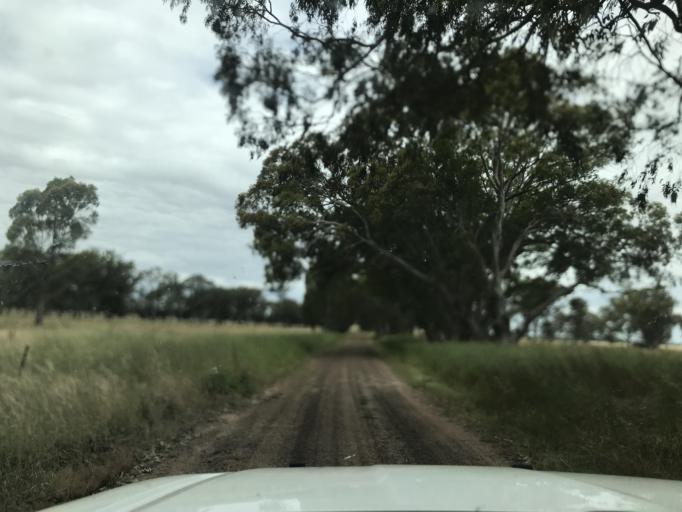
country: AU
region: South Australia
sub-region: Naracoorte and Lucindale
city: Naracoorte
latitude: -36.9250
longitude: 141.3090
